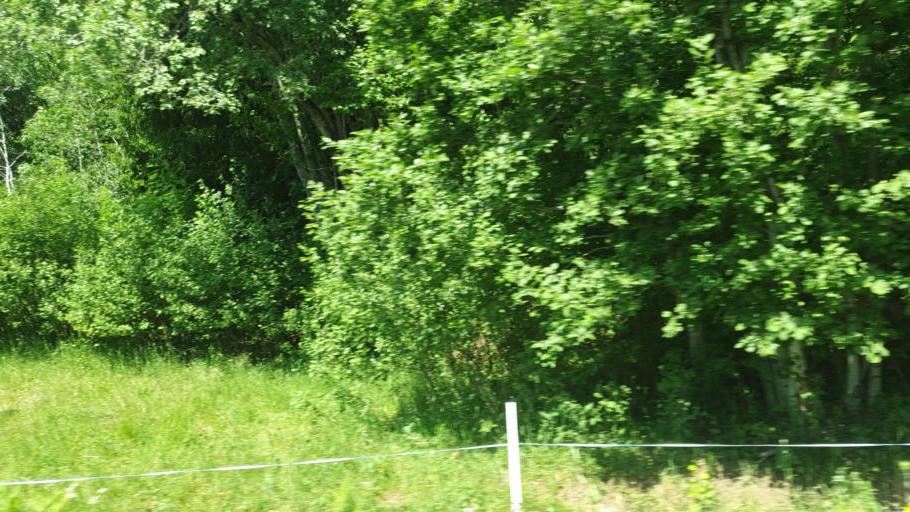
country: NO
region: Nord-Trondelag
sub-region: Leksvik
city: Leksvik
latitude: 63.6824
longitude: 10.6651
